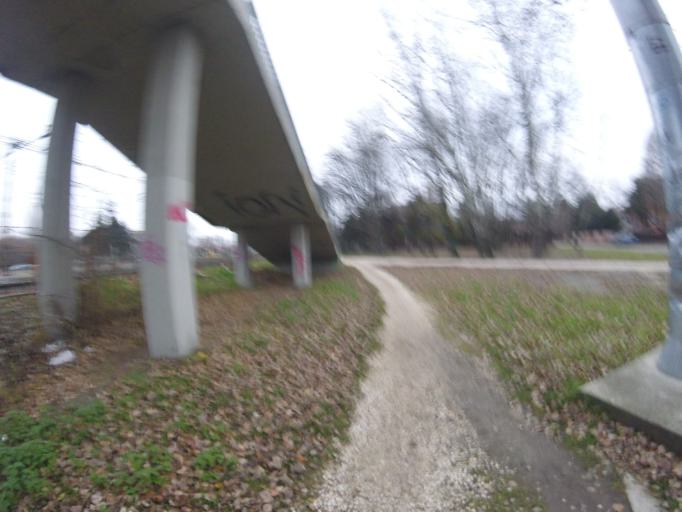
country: HU
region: Budapest
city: Budapest III. keruelet
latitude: 47.5705
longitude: 19.0477
